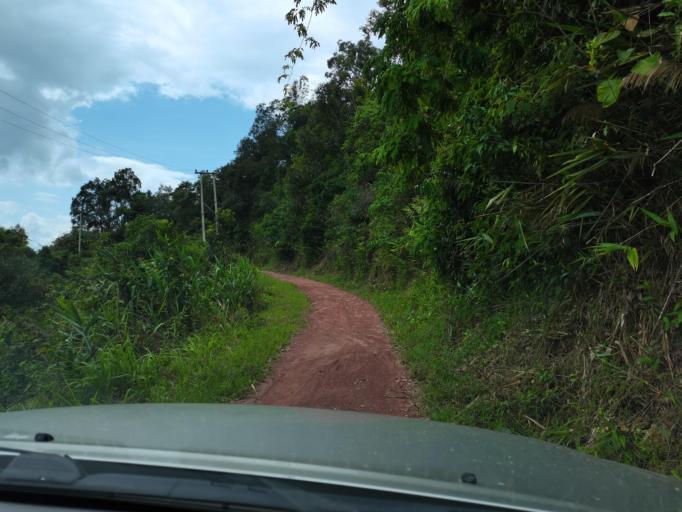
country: LA
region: Loungnamtha
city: Muang Nale
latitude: 20.5102
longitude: 101.0826
